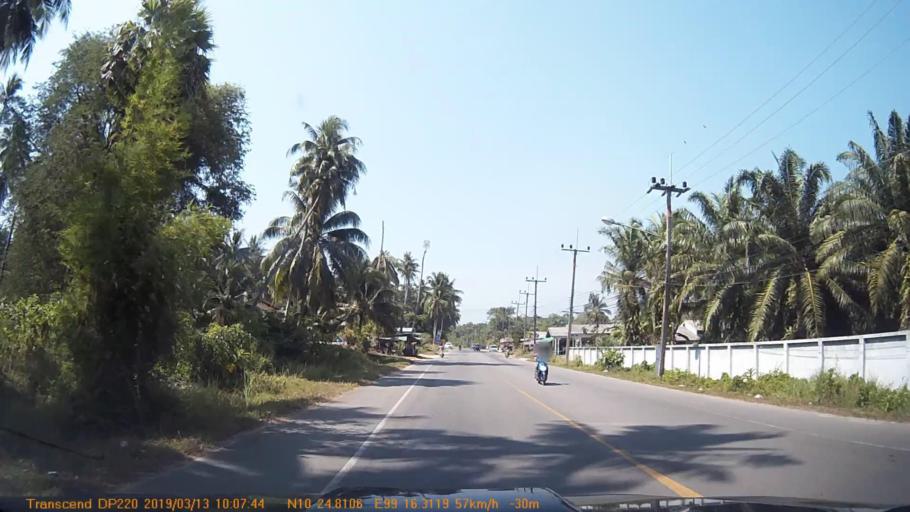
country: TH
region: Chumphon
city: Chumphon
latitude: 10.4134
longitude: 99.2718
